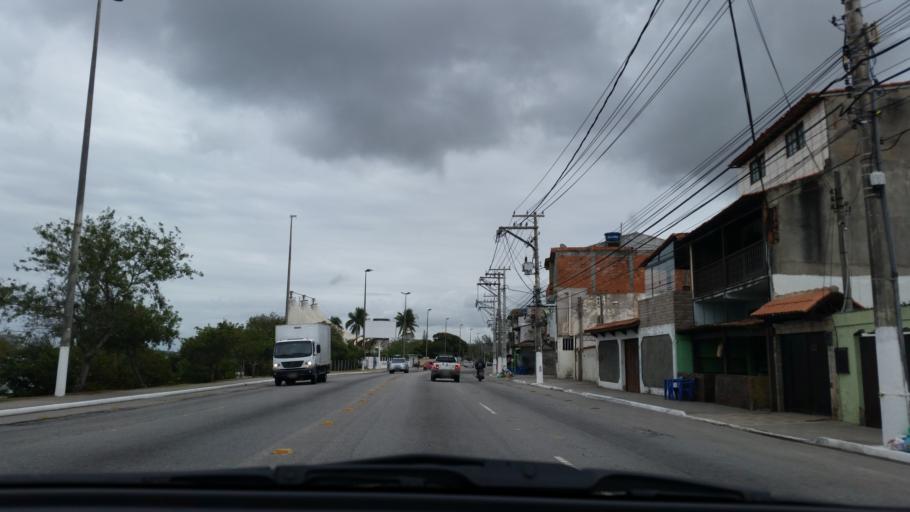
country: BR
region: Rio de Janeiro
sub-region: Cabo Frio
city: Cabo Frio
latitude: -22.8703
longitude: -42.0260
